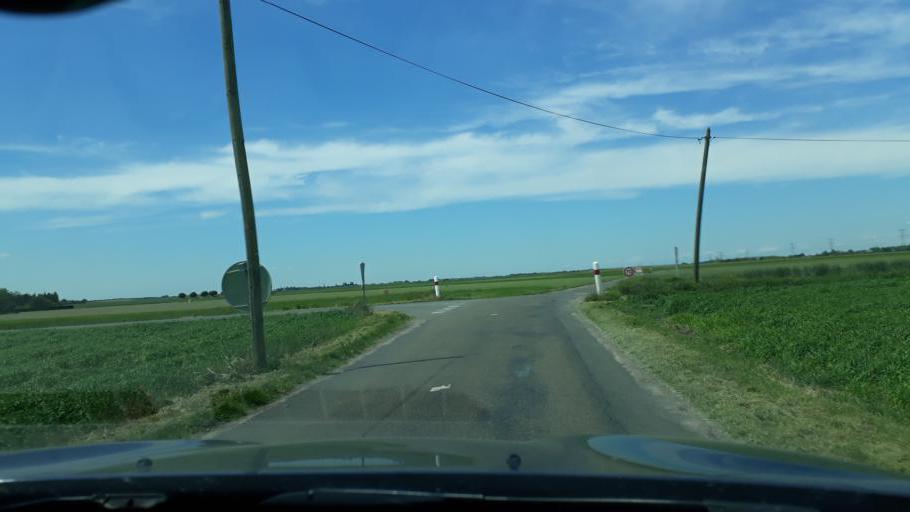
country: FR
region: Centre
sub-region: Departement du Loiret
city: Dadonville
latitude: 48.1063
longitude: 2.2417
